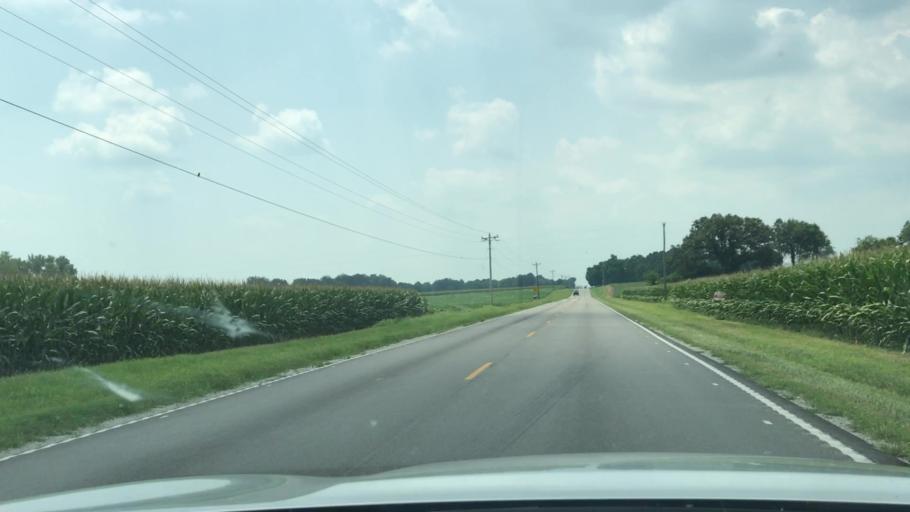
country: US
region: Kentucky
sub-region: Todd County
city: Guthrie
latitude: 36.6942
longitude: -87.1257
